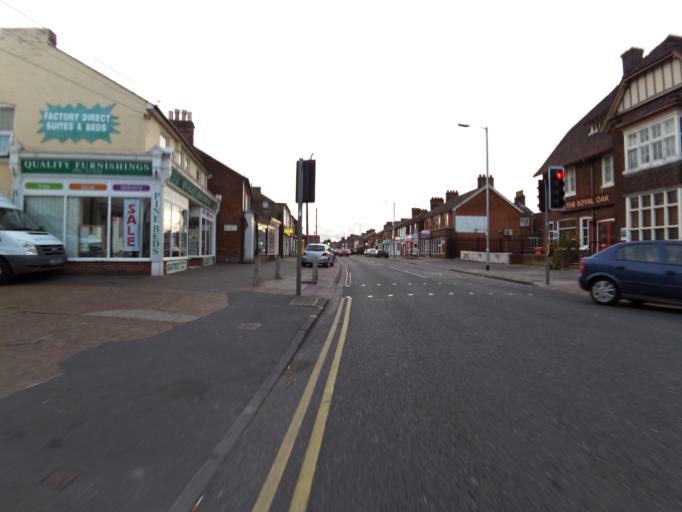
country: GB
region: England
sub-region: Suffolk
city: Ipswich
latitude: 52.0478
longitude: 1.1814
